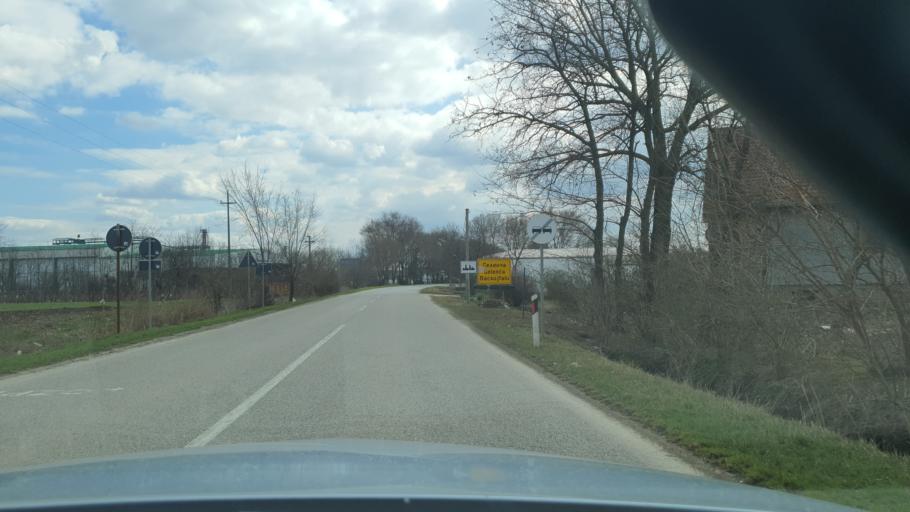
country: RS
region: Autonomna Pokrajina Vojvodina
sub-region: Juznobacki Okrug
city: Bac
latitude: 45.4210
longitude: 19.3103
